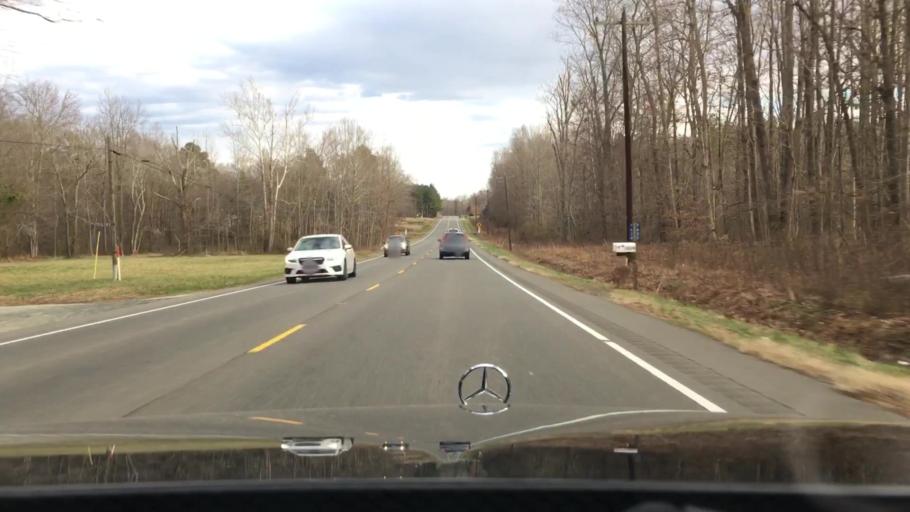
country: US
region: North Carolina
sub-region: Orange County
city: Hillsborough
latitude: 36.2062
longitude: -79.1548
